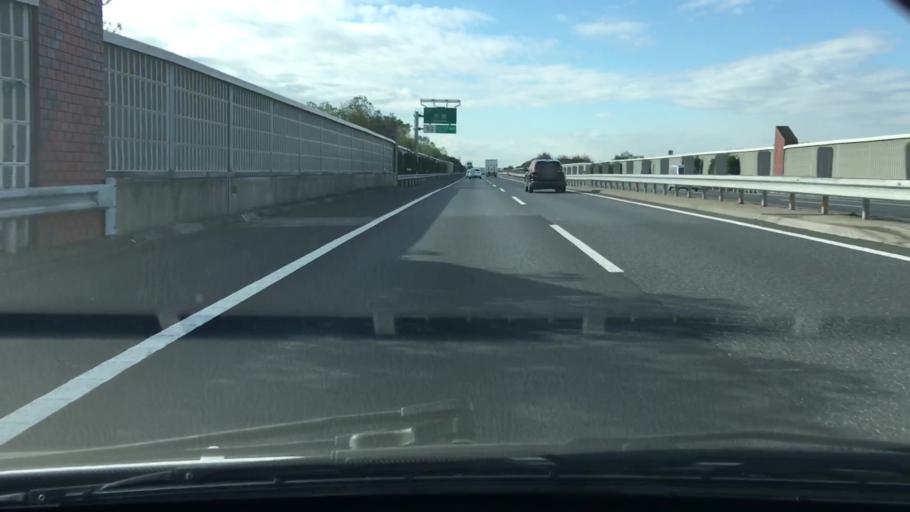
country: JP
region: Chiba
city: Ichihara
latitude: 35.5032
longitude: 140.1014
